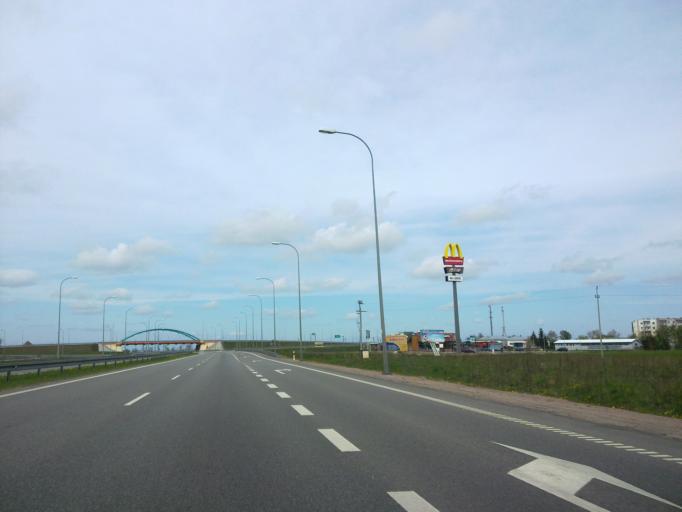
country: PL
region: Pomeranian Voivodeship
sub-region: Powiat nowodworski
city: Nowy Dwor Gdanski
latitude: 54.2116
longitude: 19.1045
